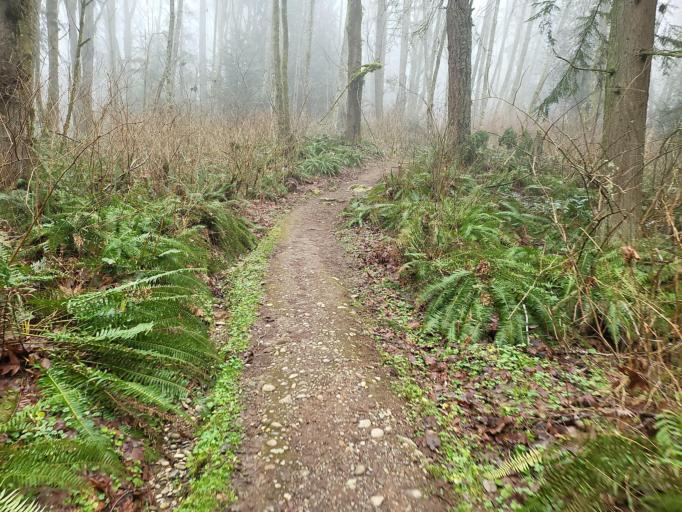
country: US
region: Washington
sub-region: King County
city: Newcastle
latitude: 47.5367
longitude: -122.1241
